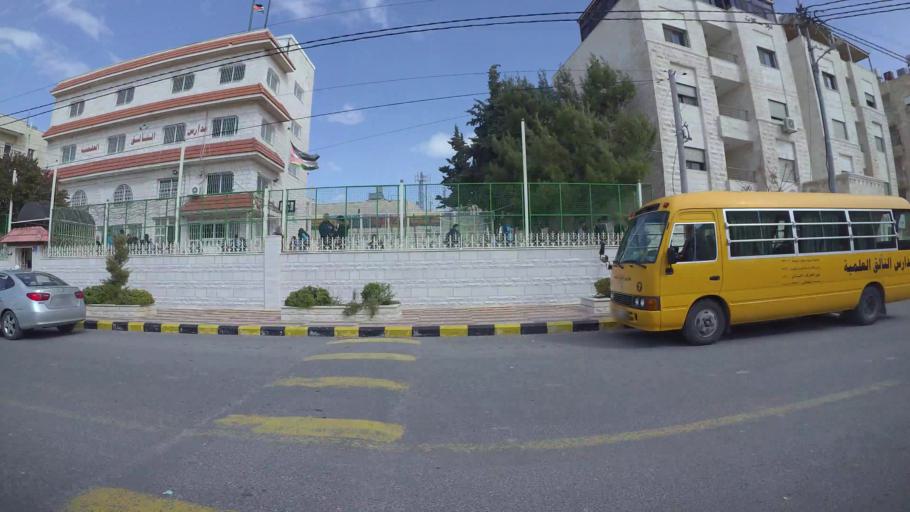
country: JO
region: Amman
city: Al Jubayhah
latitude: 32.0205
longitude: 35.8541
